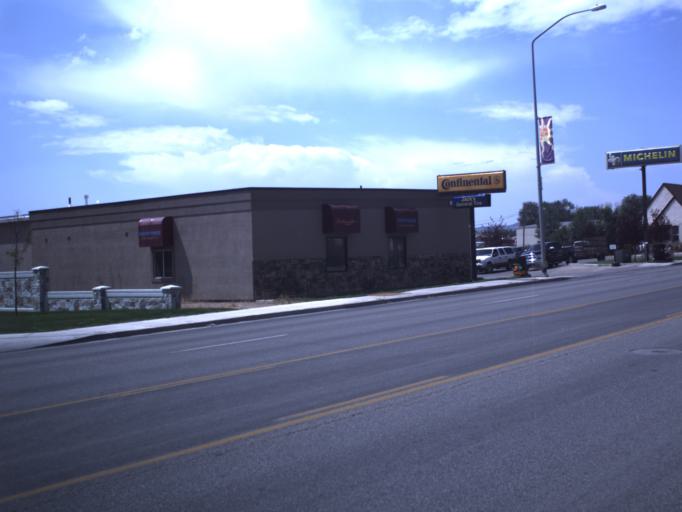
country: US
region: Utah
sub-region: Uintah County
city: Vernal
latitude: 40.4560
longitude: -109.5147
